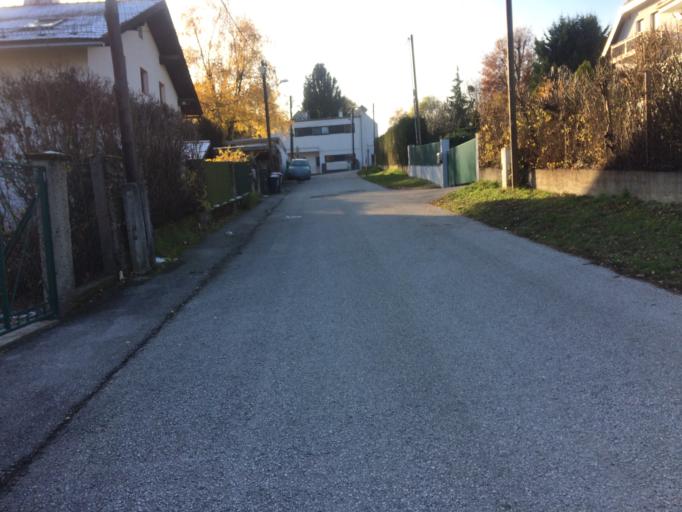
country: AT
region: Lower Austria
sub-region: Politischer Bezirk Wien-Umgebung
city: Gablitz
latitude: 48.2207
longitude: 16.1495
